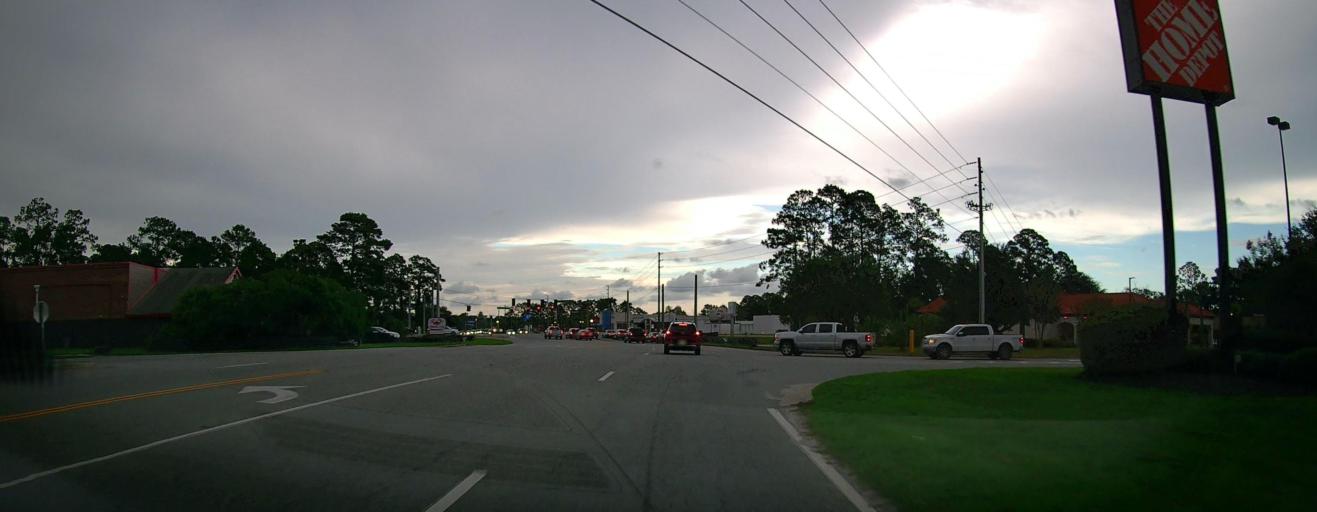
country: US
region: Georgia
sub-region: Glynn County
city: Dock Junction
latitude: 31.2125
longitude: -81.4923
